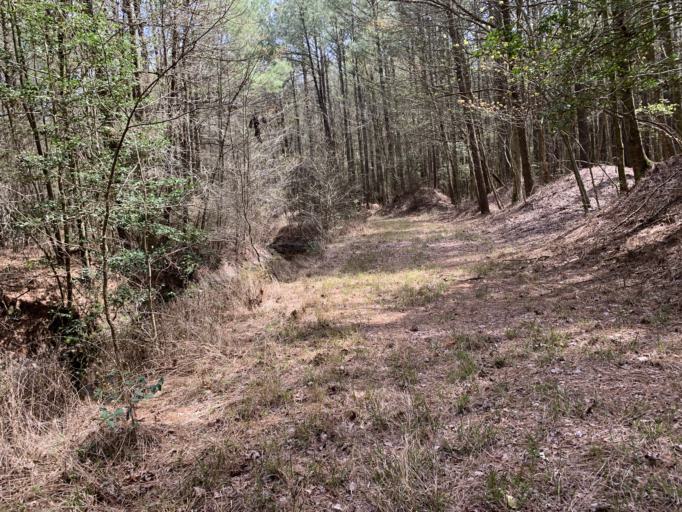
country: US
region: Delaware
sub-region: Sussex County
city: Millsboro
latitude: 38.5392
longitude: -75.3887
